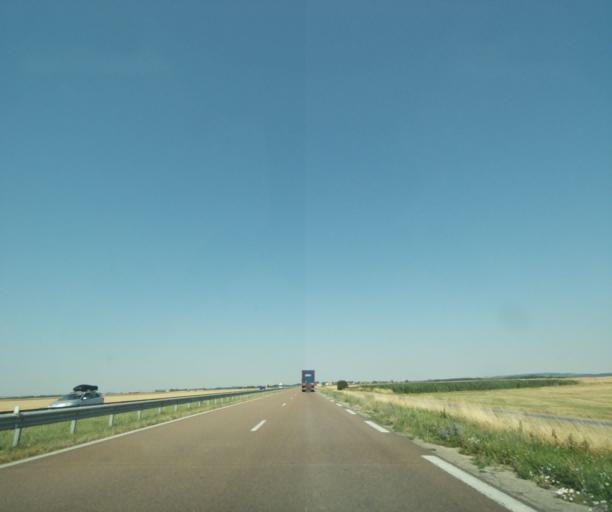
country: FR
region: Champagne-Ardenne
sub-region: Departement de la Marne
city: Frignicourt
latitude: 48.6999
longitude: 4.6812
